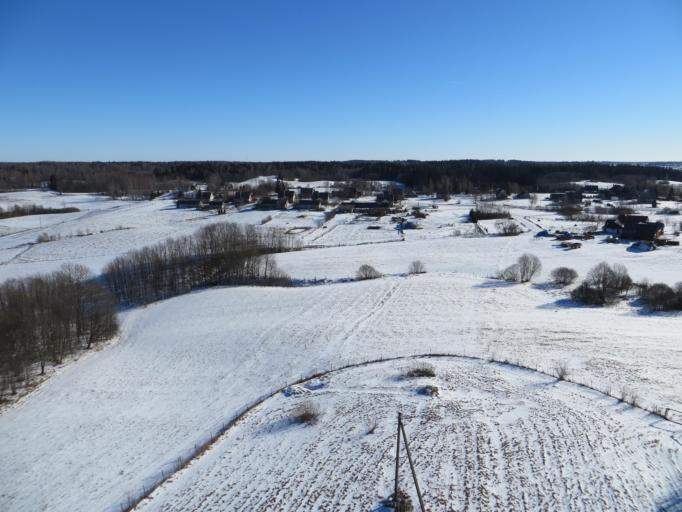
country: LT
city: Moletai
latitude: 55.3910
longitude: 25.4556
